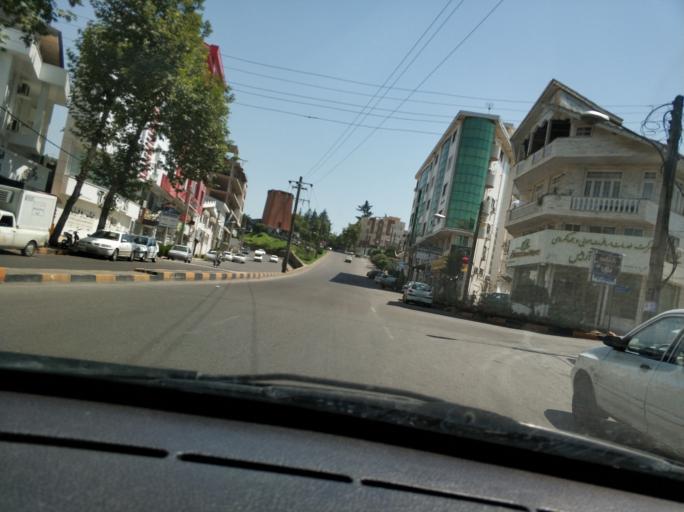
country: IR
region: Gilan
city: Lahijan
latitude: 37.1972
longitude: 50.0139
